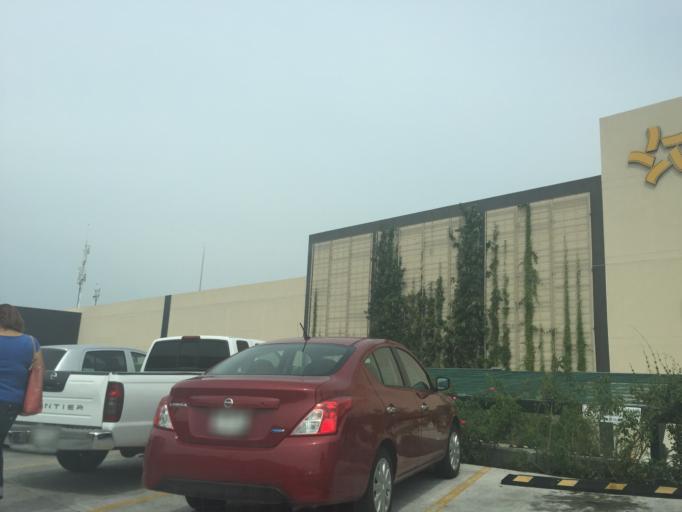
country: MX
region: Colima
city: Colima
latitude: 19.2528
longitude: -103.7199
